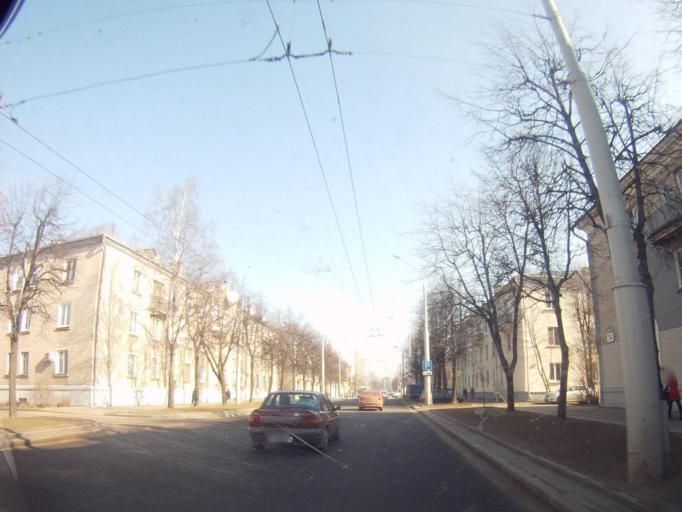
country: BY
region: Minsk
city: Minsk
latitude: 53.9264
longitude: 27.6033
